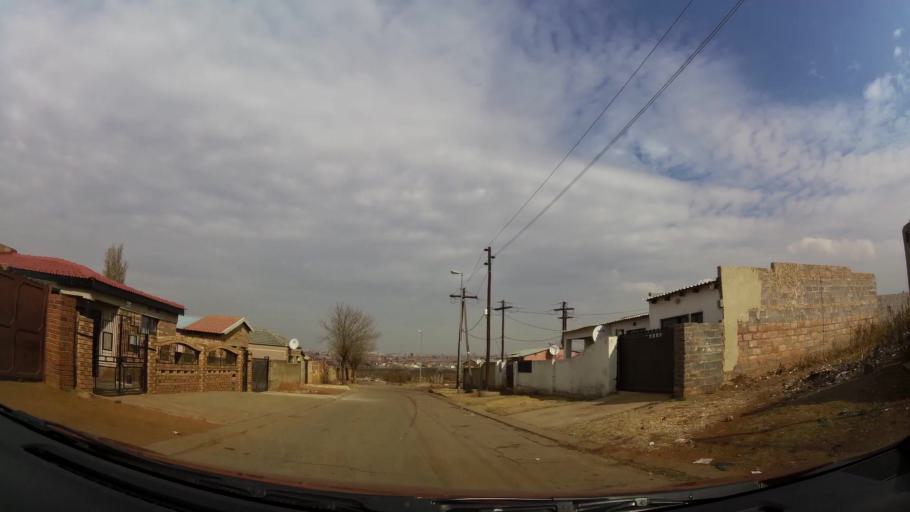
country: ZA
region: Gauteng
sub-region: City of Johannesburg Metropolitan Municipality
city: Soweto
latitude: -26.2615
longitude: 27.8203
